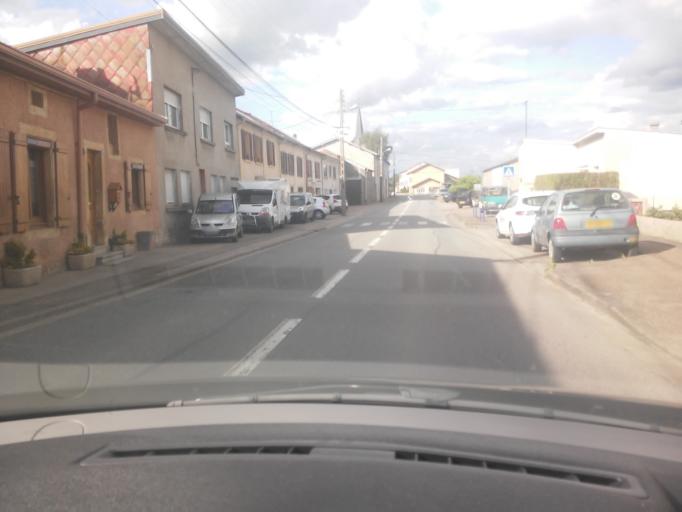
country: FR
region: Lorraine
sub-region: Departement de la Moselle
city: Marange-Silvange
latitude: 49.1972
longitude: 6.0880
